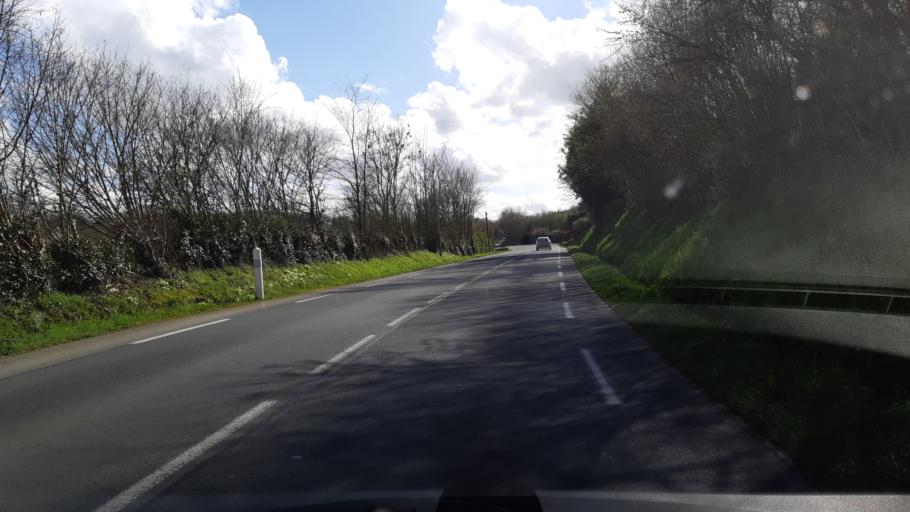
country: FR
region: Lower Normandy
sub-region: Departement de la Manche
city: Agneaux
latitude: 49.0860
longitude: -1.1146
